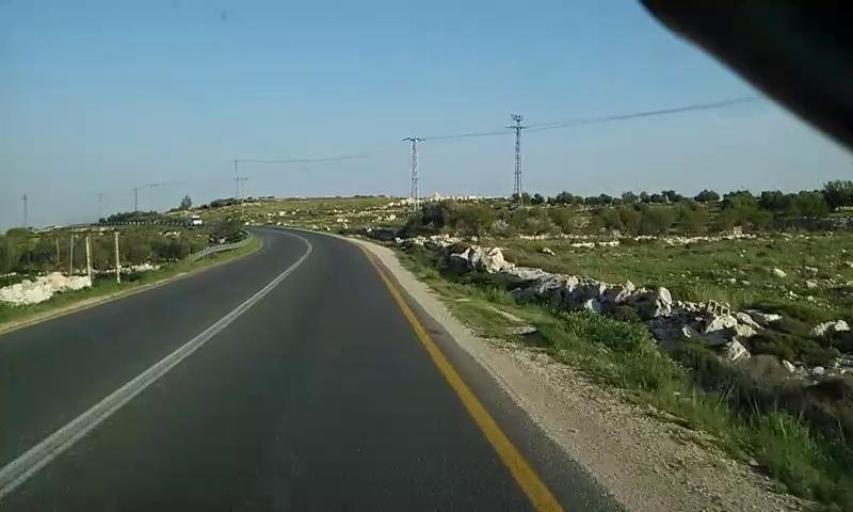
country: PS
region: West Bank
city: Marah Rabbah
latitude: 31.6467
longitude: 35.1878
